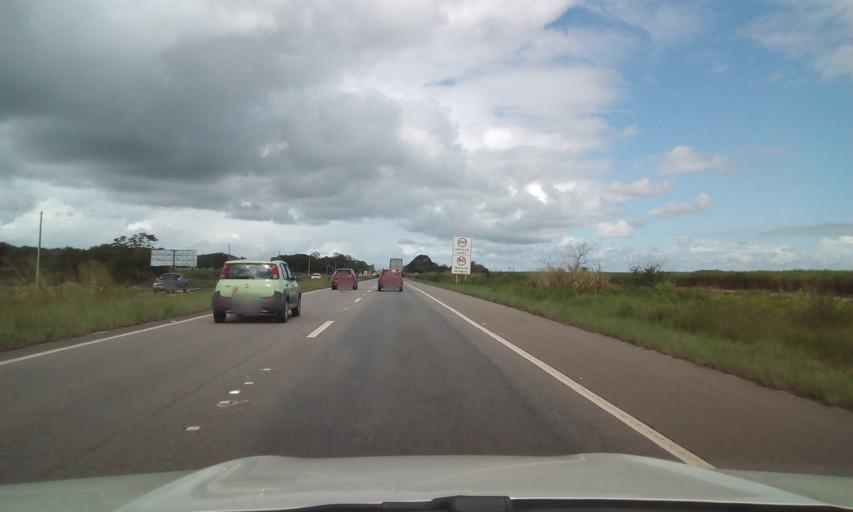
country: BR
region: Pernambuco
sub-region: Goiana
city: Goiana
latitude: -7.6363
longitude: -34.9593
